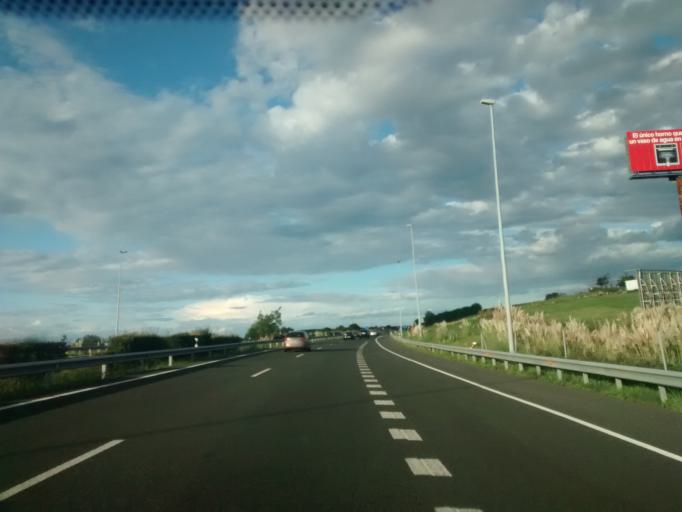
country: ES
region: Cantabria
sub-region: Provincia de Cantabria
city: Santa Cruz de Bezana
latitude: 43.4440
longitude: -3.8899
